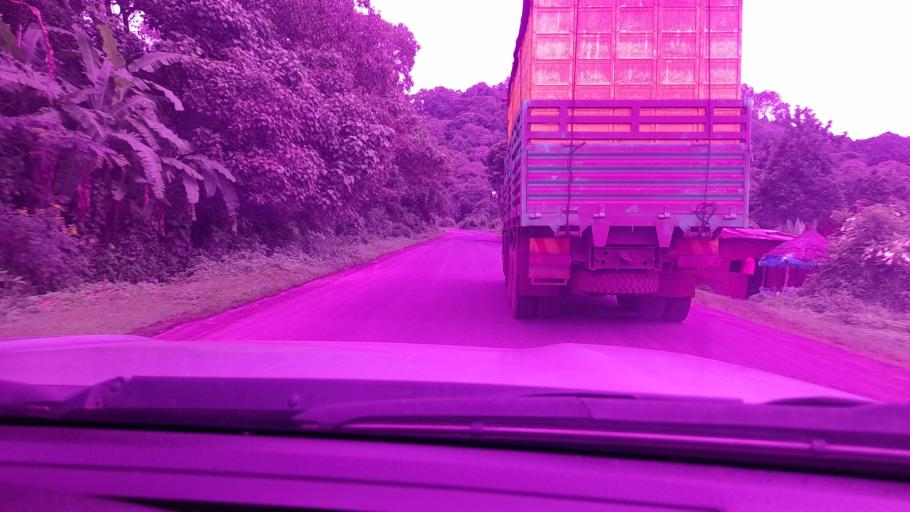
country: ET
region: Oromiya
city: Jima
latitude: 7.6589
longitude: 36.8808
